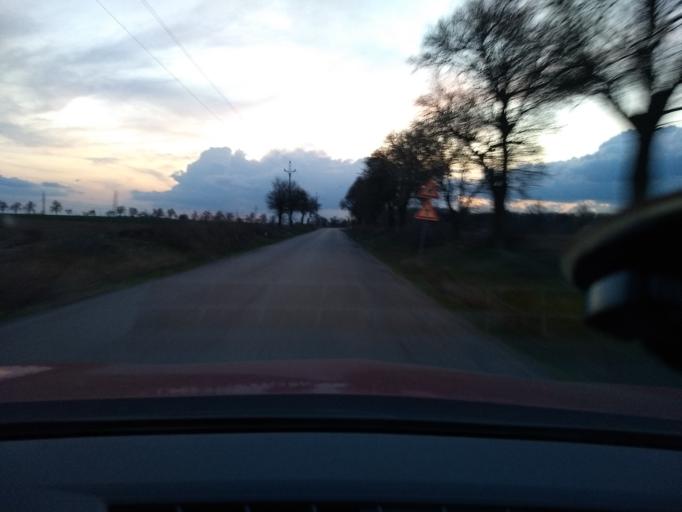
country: CZ
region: Central Bohemia
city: Jenec
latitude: 50.0671
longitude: 14.1932
